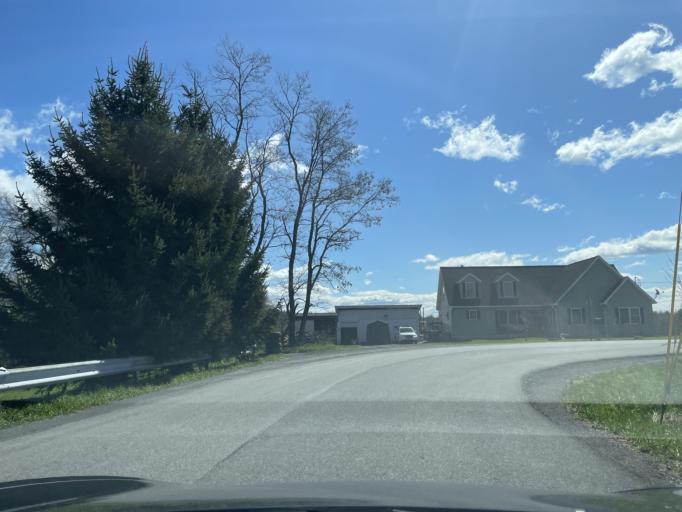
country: US
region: New York
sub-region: Ulster County
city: Saugerties South
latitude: 42.0460
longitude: -73.9914
